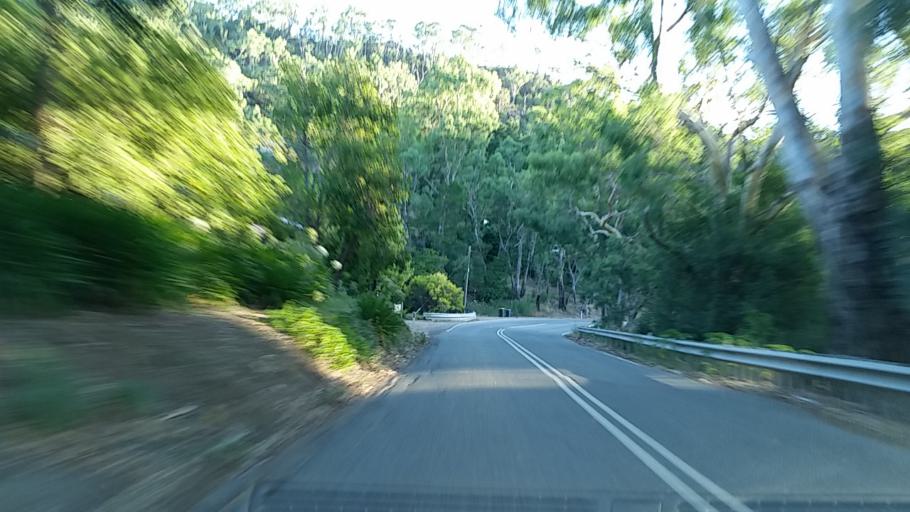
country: AU
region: South Australia
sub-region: Campbelltown
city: Athelstone
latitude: -34.8679
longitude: 138.7565
